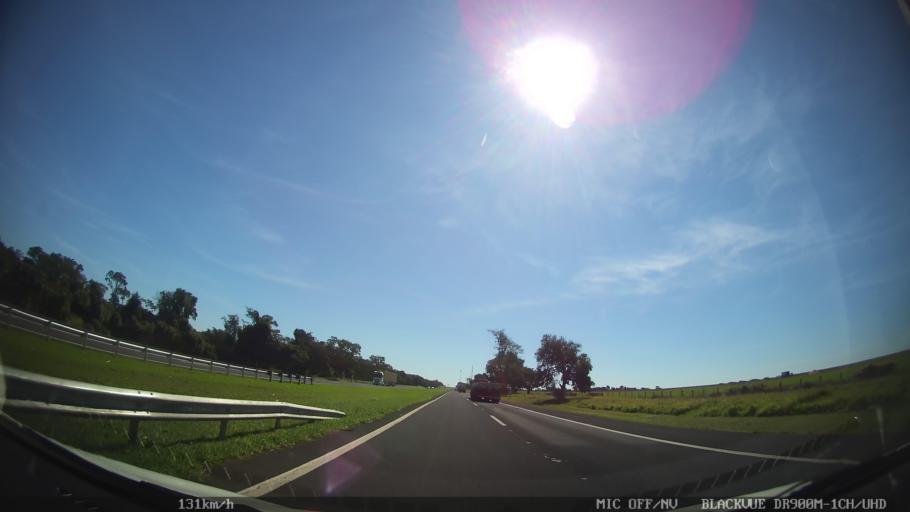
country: BR
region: Sao Paulo
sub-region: Santa Rita Do Passa Quatro
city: Santa Rita do Passa Quatro
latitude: -21.6325
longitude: -47.6132
